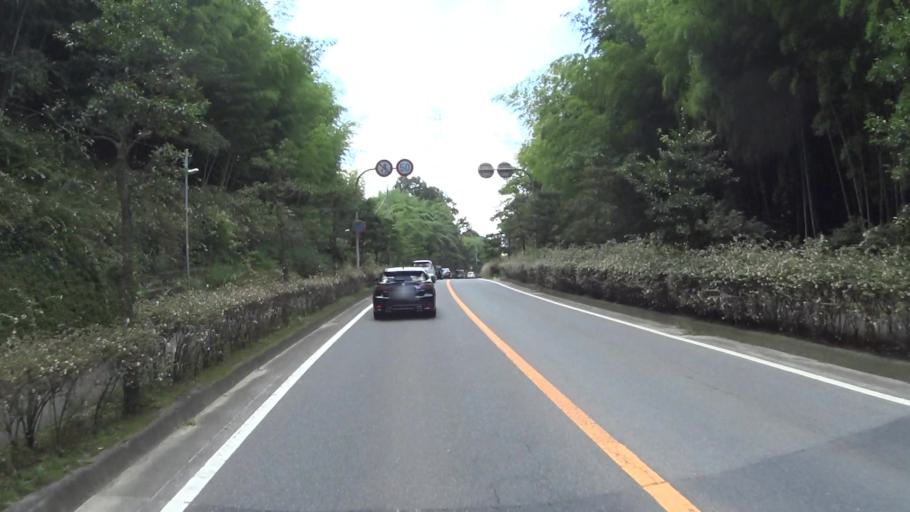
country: JP
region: Kyoto
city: Tanabe
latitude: 34.8494
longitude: 135.7915
